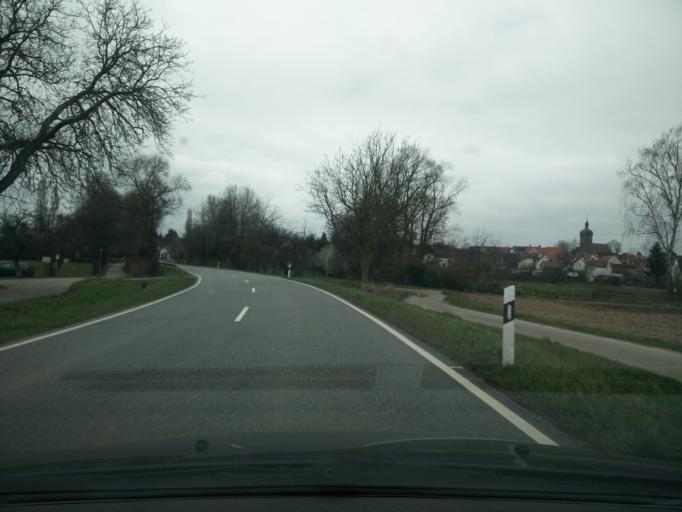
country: DE
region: Rheinland-Pfalz
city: Billigheim-Ingenheim
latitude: 49.1415
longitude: 8.1002
